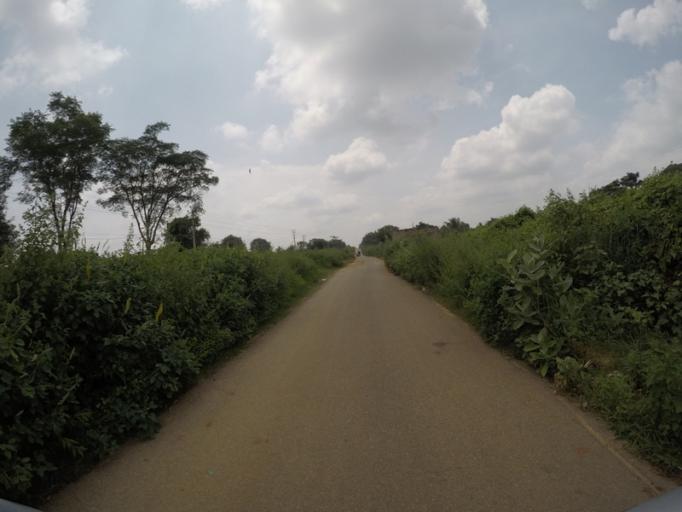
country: IN
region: Karnataka
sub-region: Ramanagara
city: Kanakapura
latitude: 12.6918
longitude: 77.4657
